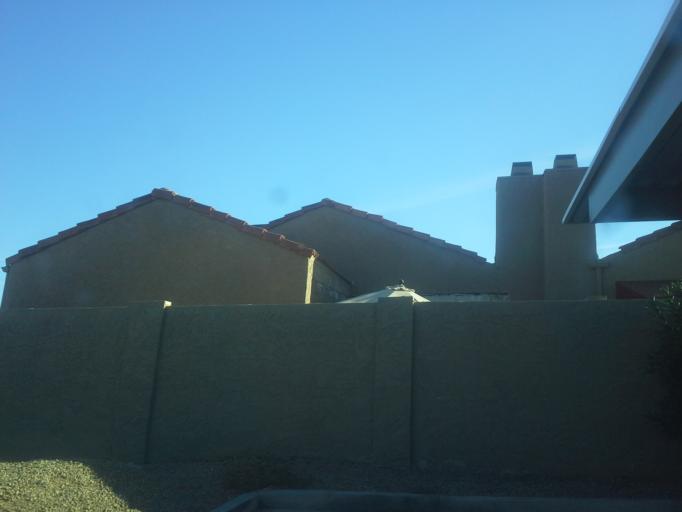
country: US
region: Arizona
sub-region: Maricopa County
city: Paradise Valley
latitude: 33.6238
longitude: -111.9964
